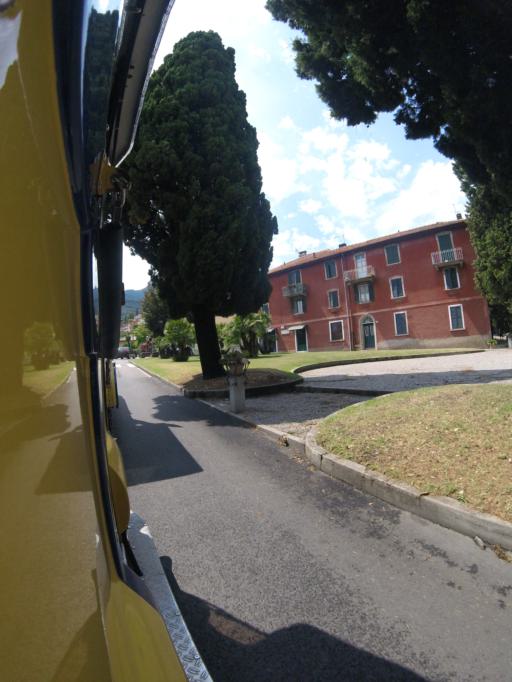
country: IT
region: Lombardy
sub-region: Provincia di Como
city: Griante
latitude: 46.0078
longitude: 9.2346
